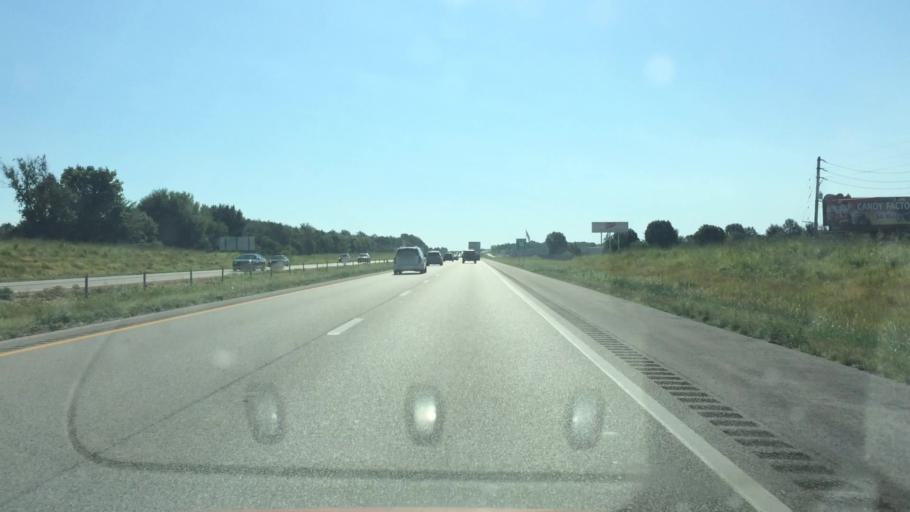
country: US
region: Missouri
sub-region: Greene County
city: Strafford
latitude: 37.2501
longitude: -93.2072
